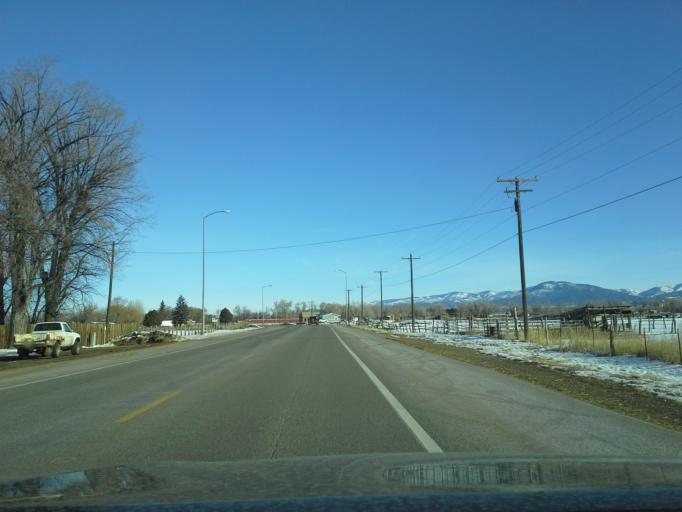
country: US
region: Utah
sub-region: Beaver County
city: Beaver
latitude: 38.2591
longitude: -112.6451
